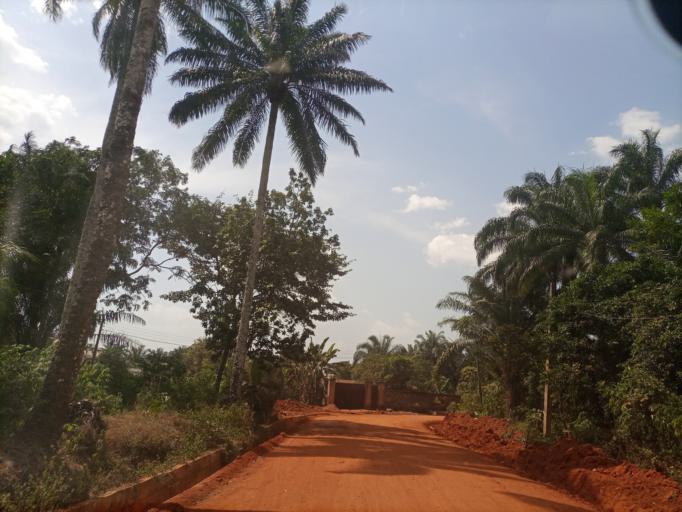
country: NG
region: Enugu
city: Obollo-Afor
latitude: 6.8669
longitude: 7.4728
